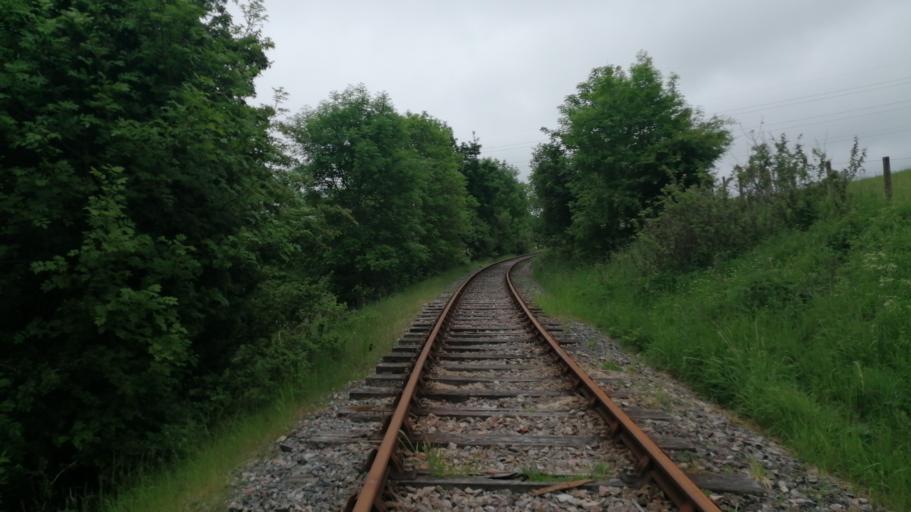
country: GB
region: Scotland
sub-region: Moray
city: Keith
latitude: 57.5359
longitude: -2.9617
